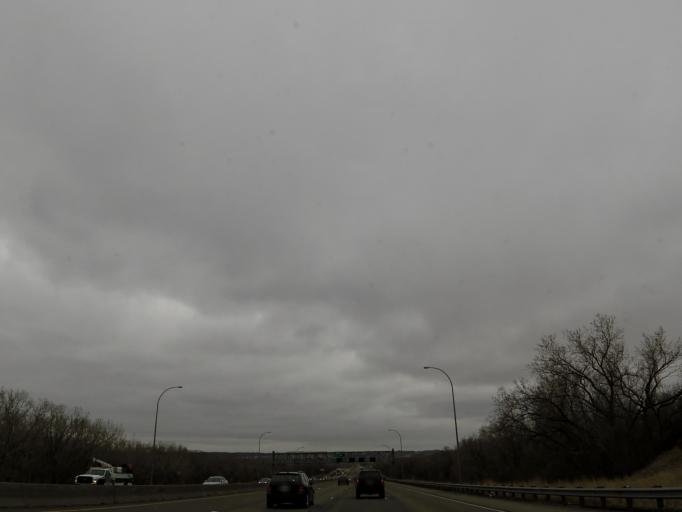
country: US
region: Minnesota
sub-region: Hennepin County
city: Bloomington
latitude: 44.8065
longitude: -93.2913
